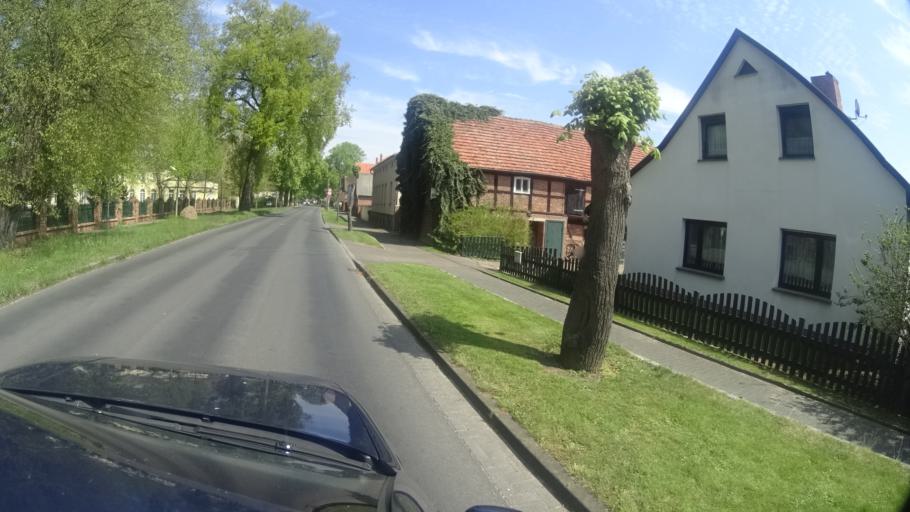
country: DE
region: Brandenburg
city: Wusterhausen
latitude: 52.8642
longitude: 12.4568
